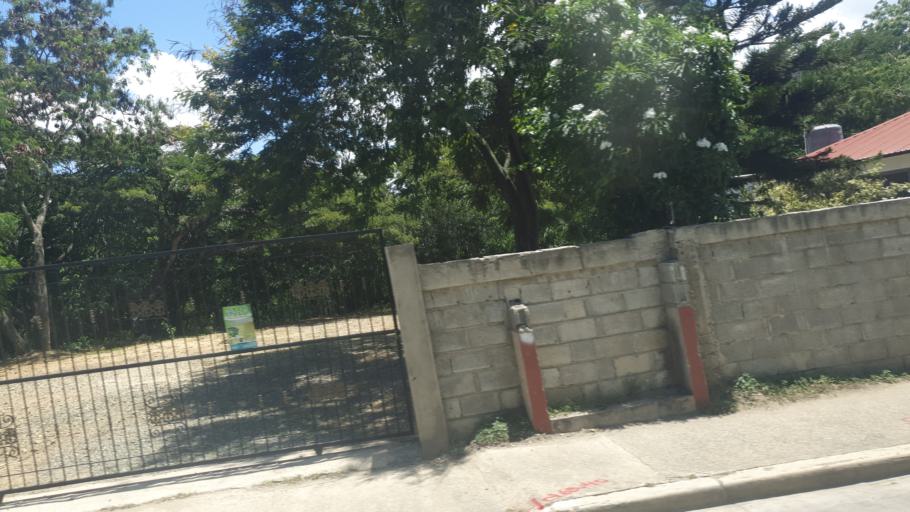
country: DO
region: Santiago
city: Santiago de los Caballeros
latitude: 19.4258
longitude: -70.6747
